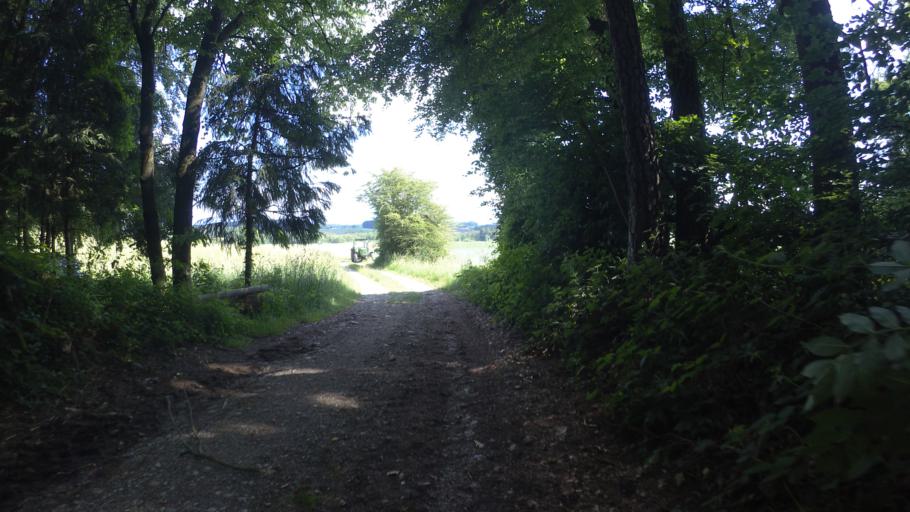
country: DE
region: Bavaria
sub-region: Upper Bavaria
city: Chieming
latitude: 47.9431
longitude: 12.5220
